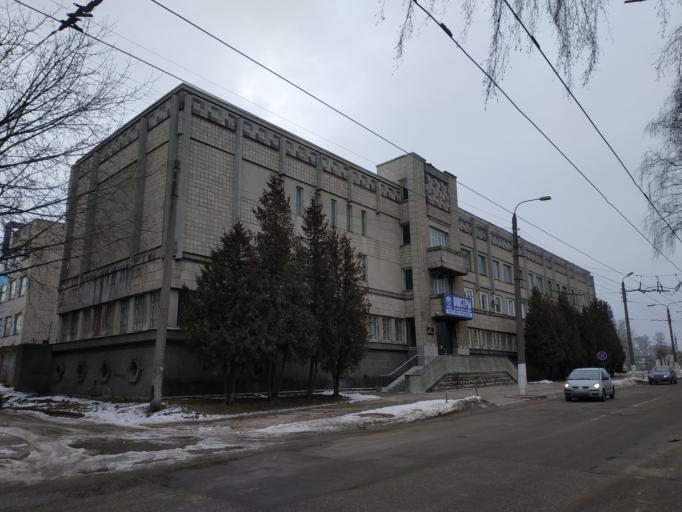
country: RU
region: Tverskaya
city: Tver
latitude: 56.8488
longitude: 35.9357
